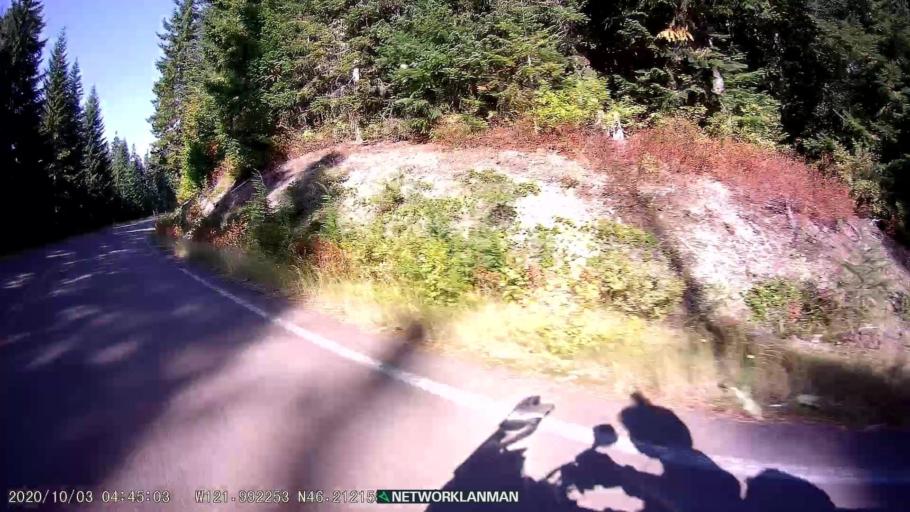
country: US
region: Washington
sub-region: Lewis County
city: Morton
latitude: 46.2123
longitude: -121.9925
